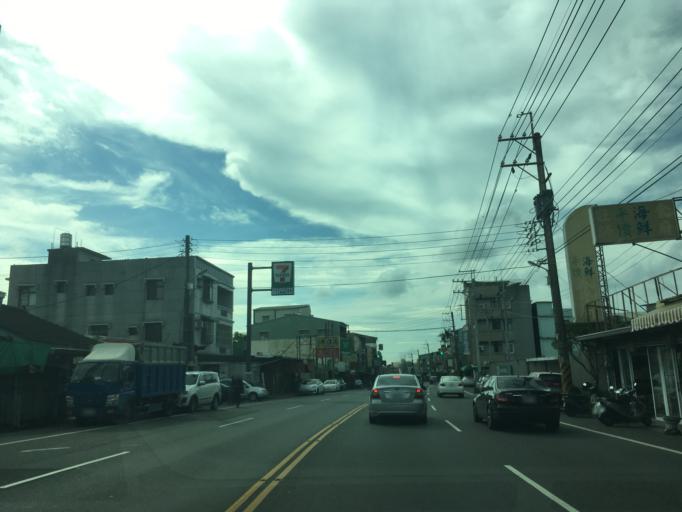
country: TW
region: Taiwan
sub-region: Chiayi
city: Jiayi Shi
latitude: 23.4465
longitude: 120.4935
